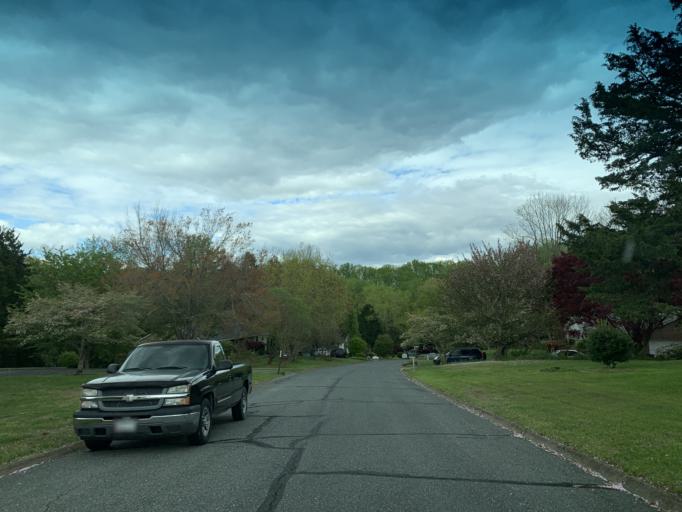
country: US
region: Maryland
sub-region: Harford County
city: Pleasant Hills
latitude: 39.4972
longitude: -76.3607
